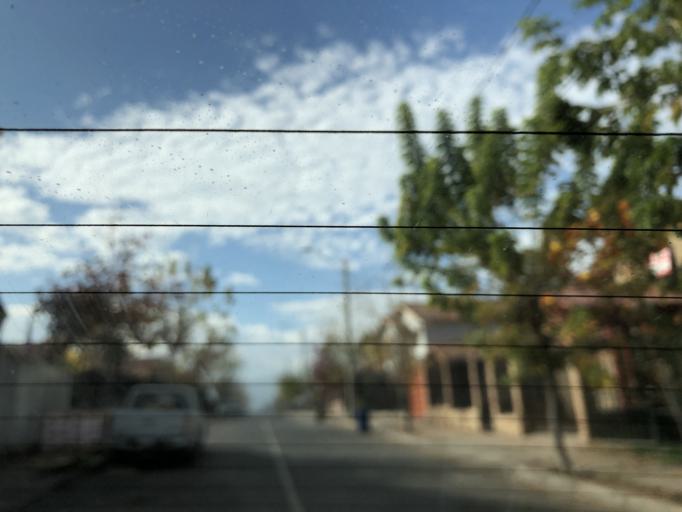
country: CL
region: Santiago Metropolitan
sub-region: Provincia de Cordillera
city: Puente Alto
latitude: -33.5881
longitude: -70.5324
